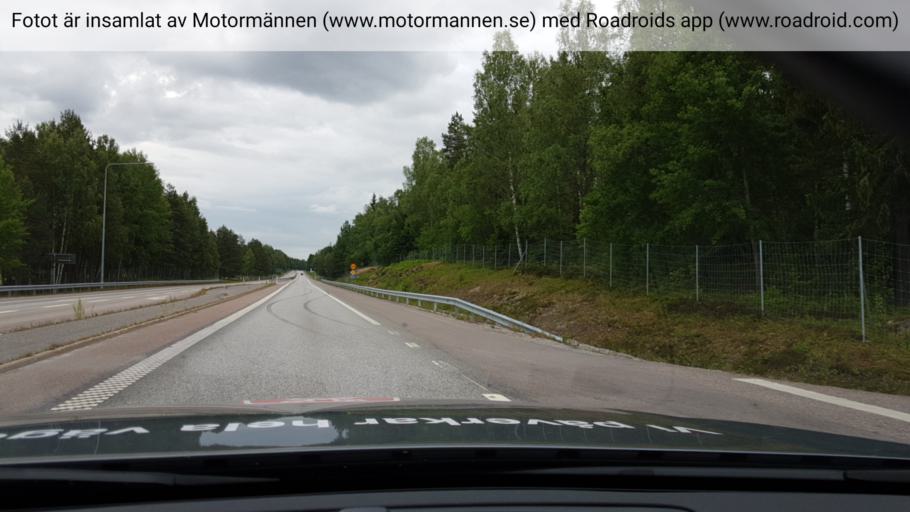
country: SE
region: Vaestmanland
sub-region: Surahammars Kommun
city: Surahammar
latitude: 59.7235
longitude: 16.2351
